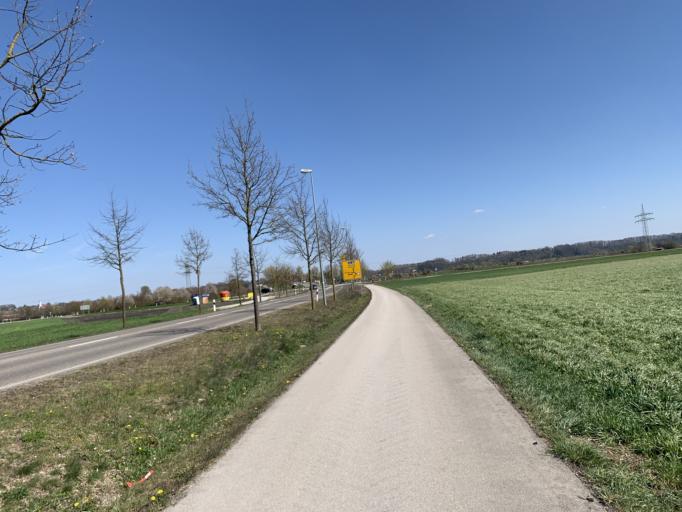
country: DE
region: Bavaria
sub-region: Swabia
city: Friedberg
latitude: 48.3831
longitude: 10.9542
